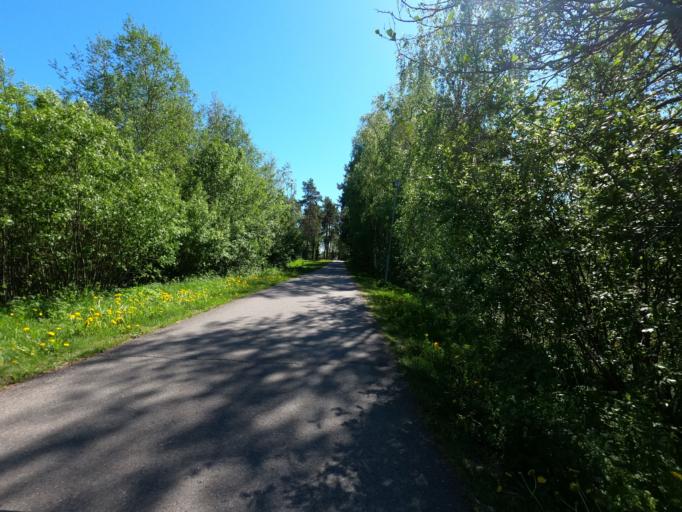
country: FI
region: North Karelia
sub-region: Joensuu
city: Joensuu
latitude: 62.5789
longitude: 29.7660
